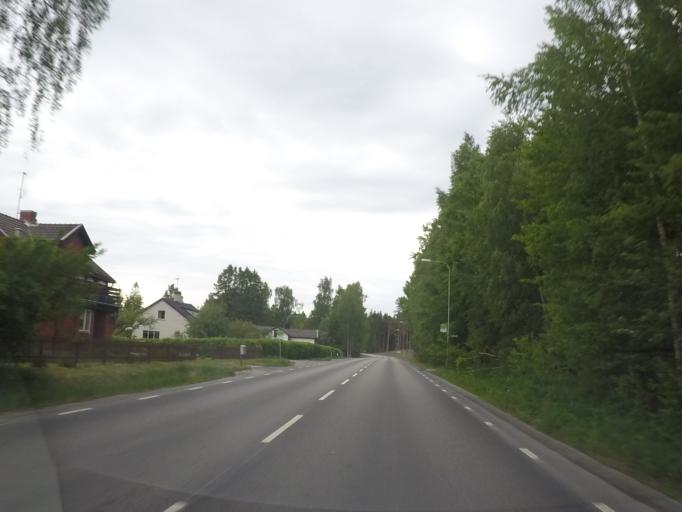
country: SE
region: Soedermanland
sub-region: Eskilstuna Kommun
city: Arla
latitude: 59.2925
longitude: 16.6766
